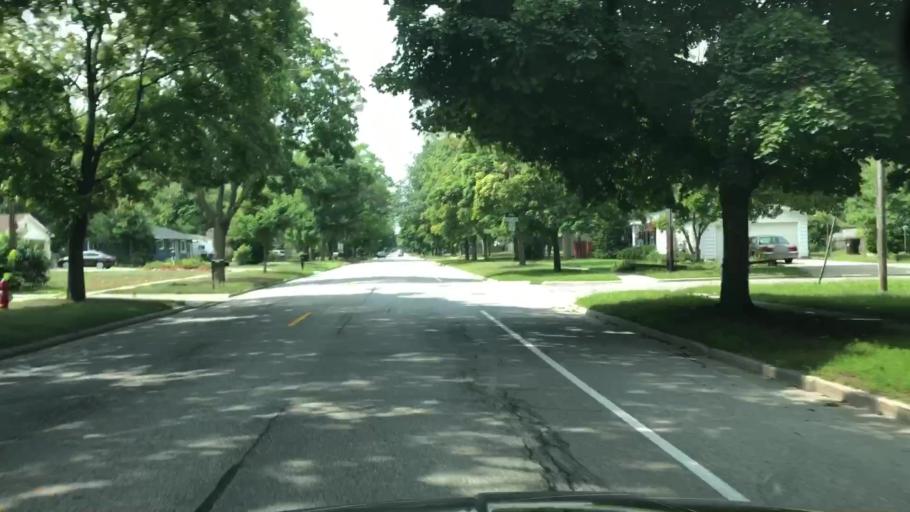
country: US
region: Michigan
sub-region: Midland County
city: Midland
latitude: 43.6266
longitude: -84.1988
